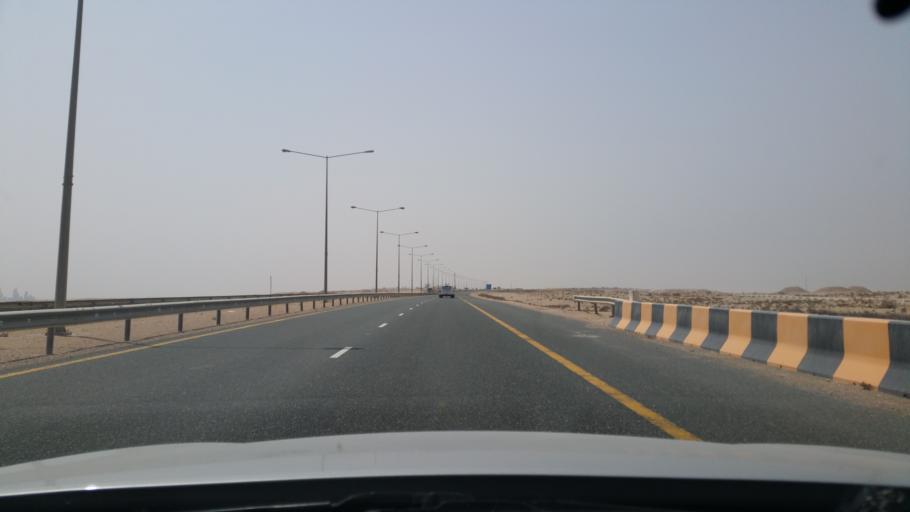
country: QA
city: Umm Bab
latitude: 25.2448
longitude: 50.8003
